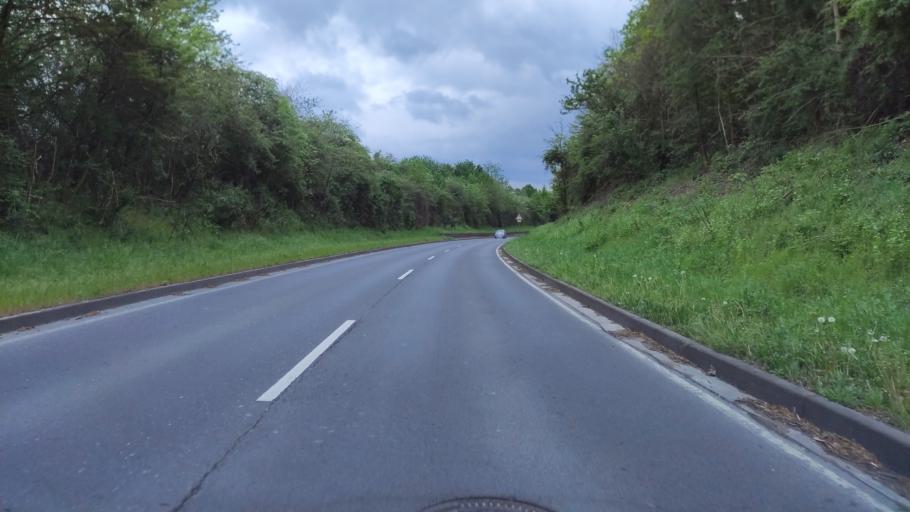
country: DE
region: North Rhine-Westphalia
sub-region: Regierungsbezirk Dusseldorf
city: Kaarst
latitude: 51.1995
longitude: 6.6189
